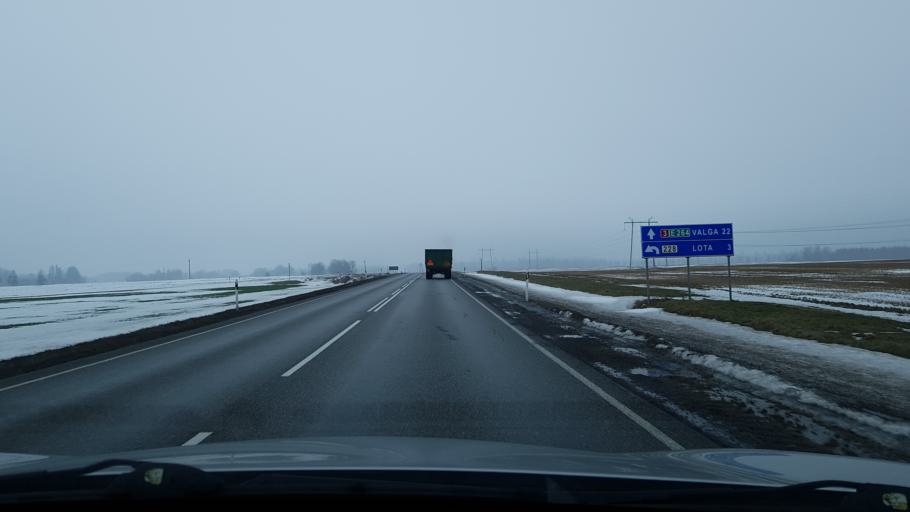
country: EE
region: Valgamaa
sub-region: Valga linn
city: Valga
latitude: 57.9438
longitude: 26.1686
